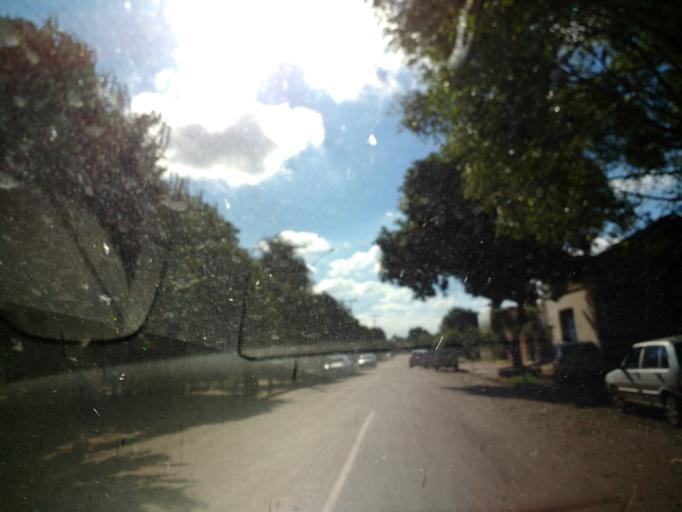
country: BR
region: Parana
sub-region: Palotina
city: Palotina
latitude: -24.4124
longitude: -53.5245
